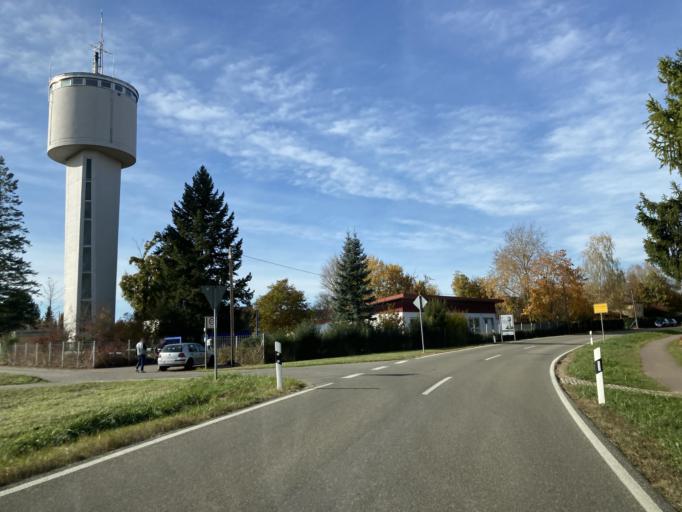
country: DE
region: Baden-Wuerttemberg
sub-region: Tuebingen Region
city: Bodelshausen
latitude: 48.3793
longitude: 8.9741
